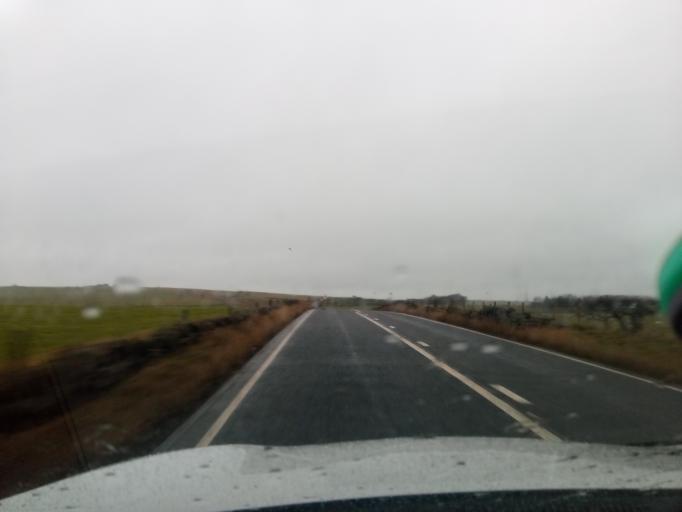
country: GB
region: Scotland
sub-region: South Lanarkshire
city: Lanark
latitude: 55.7078
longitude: -3.7286
